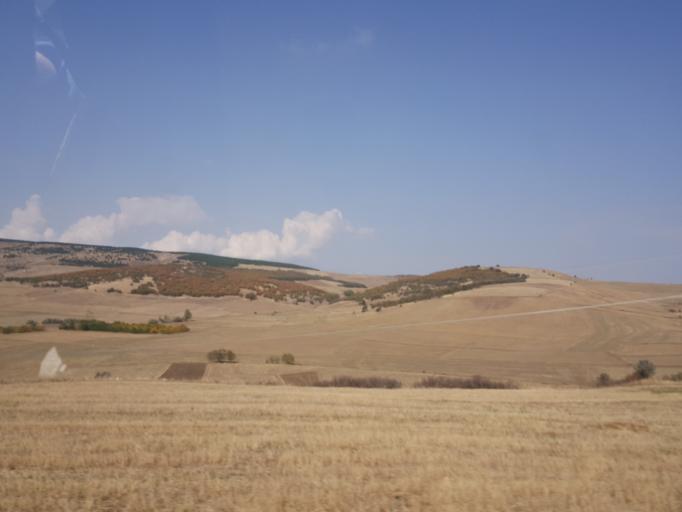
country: TR
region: Corum
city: Bogazkale
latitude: 40.1644
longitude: 34.6629
